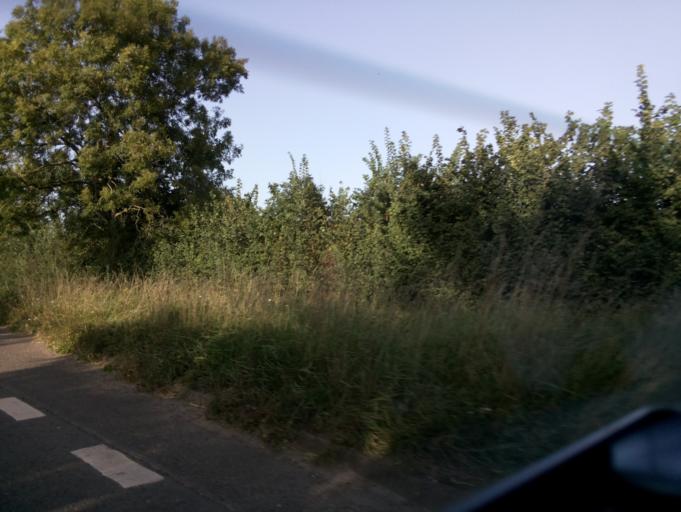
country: GB
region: England
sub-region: Gloucestershire
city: Gloucester
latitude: 51.9485
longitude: -2.3007
